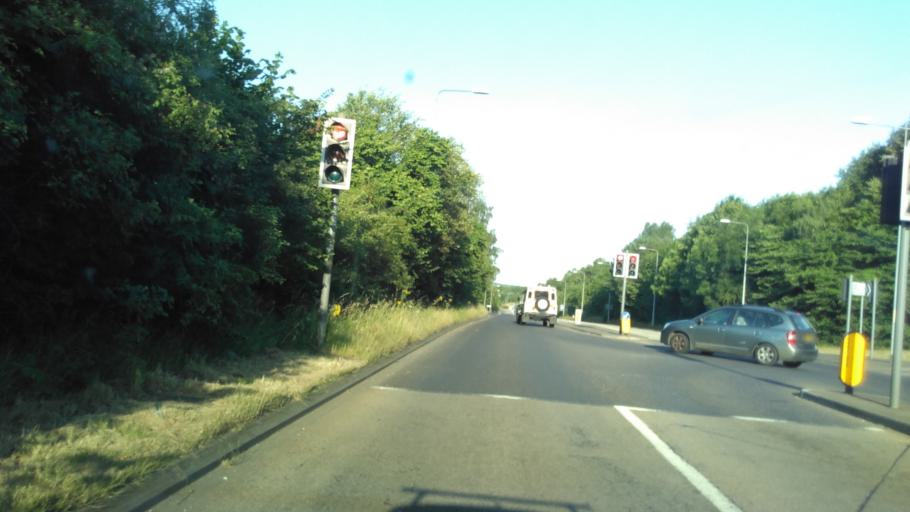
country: GB
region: England
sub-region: Kent
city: Blean
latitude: 51.2832
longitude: 1.0480
